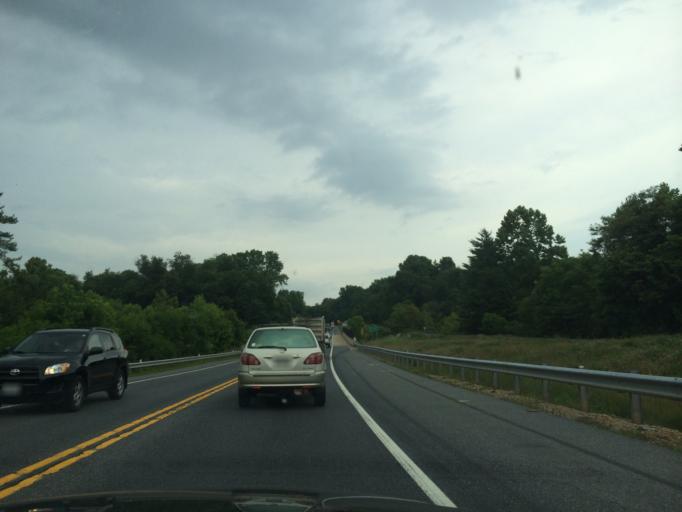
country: US
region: Maryland
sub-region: Carroll County
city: Sykesville
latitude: 39.3613
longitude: -76.9679
